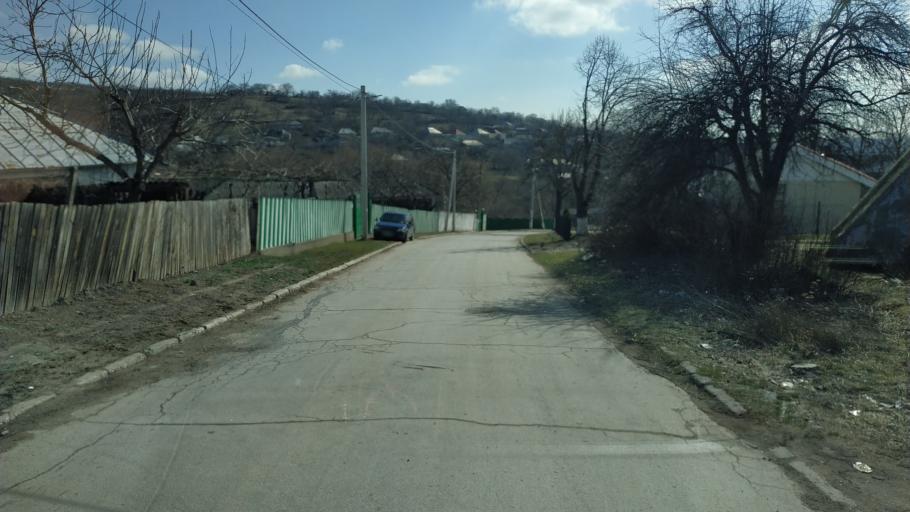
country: MD
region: Straseni
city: Straseni
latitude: 47.0190
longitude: 28.5440
